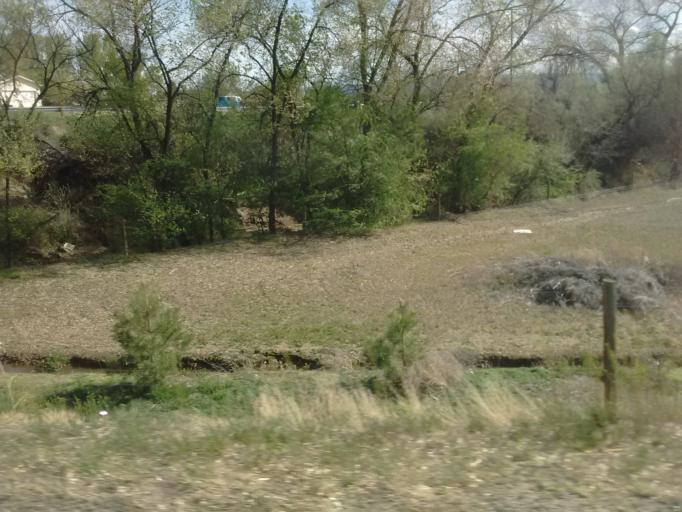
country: US
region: Colorado
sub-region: Mesa County
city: Grand Junction
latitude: 39.1063
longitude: -108.5801
